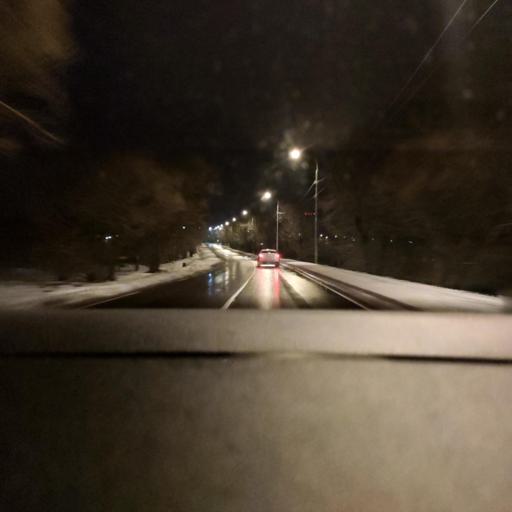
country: RU
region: Moskovskaya
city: Poselok Mar'ino
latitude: 55.5483
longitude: 37.3107
